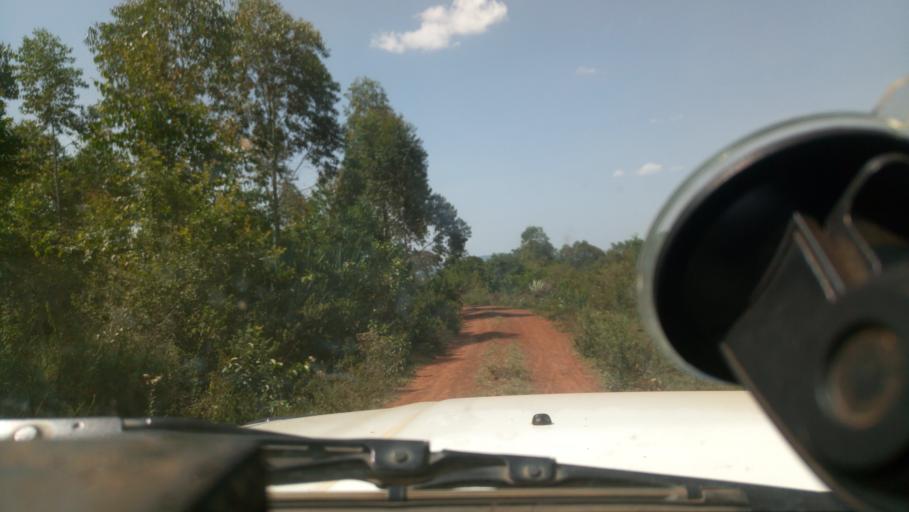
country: KE
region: Migori
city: Kihancha
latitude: -1.2072
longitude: 34.6274
